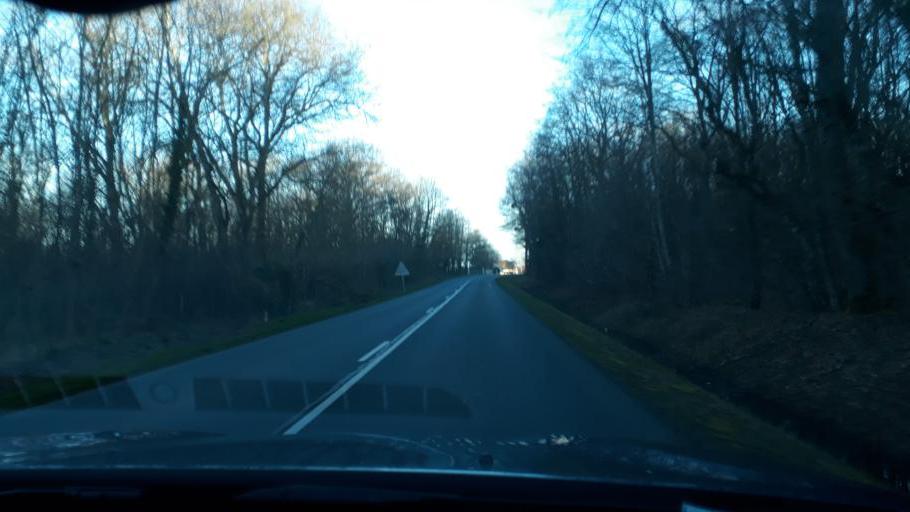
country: FR
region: Centre
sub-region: Departement du Loiret
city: Neuville-aux-Bois
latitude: 48.0443
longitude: 2.0500
